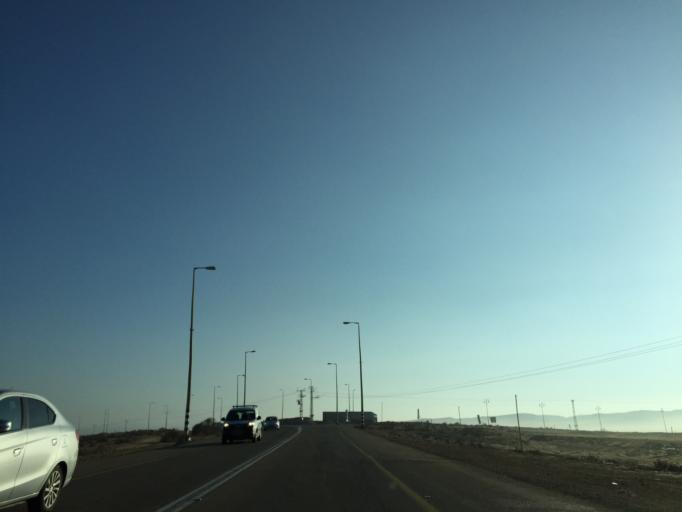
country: IL
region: Southern District
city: Yeroham
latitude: 30.9977
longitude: 34.9396
